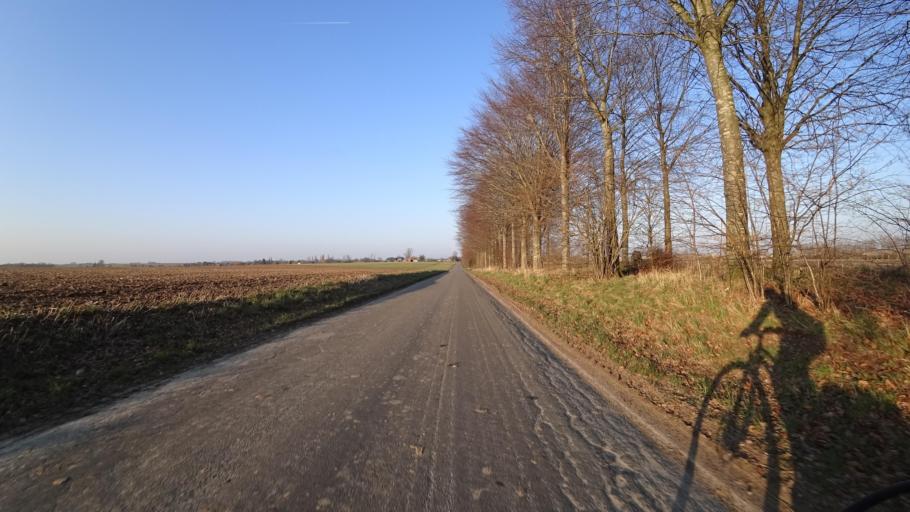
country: BE
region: Wallonia
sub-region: Province du Brabant Wallon
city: Chastre-Villeroux-Blanmont
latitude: 50.5829
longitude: 4.6682
